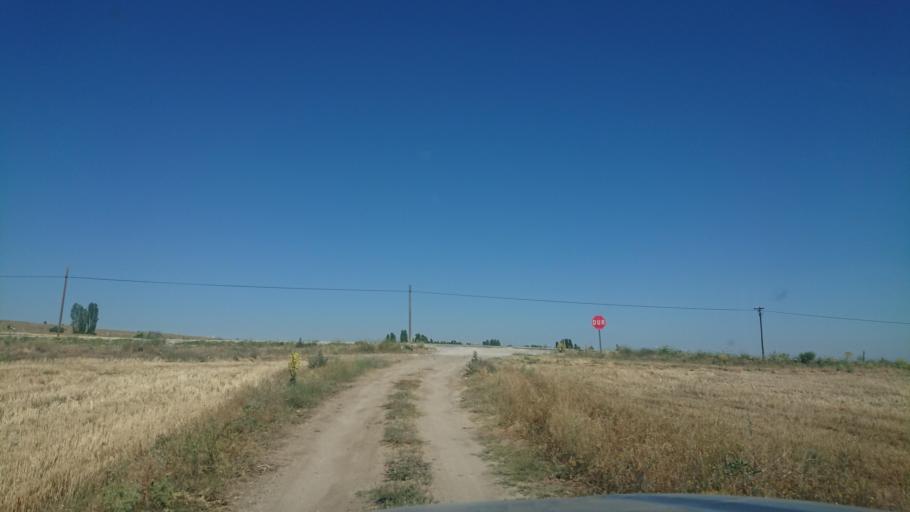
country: TR
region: Aksaray
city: Sariyahsi
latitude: 38.9398
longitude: 33.8345
